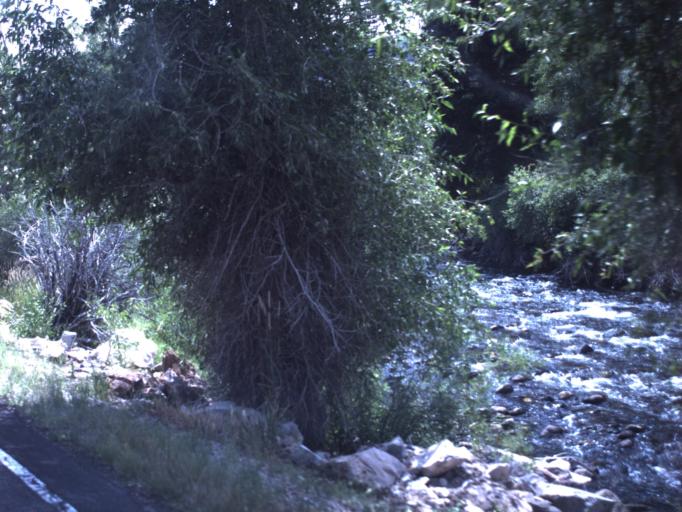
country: US
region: Utah
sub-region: Summit County
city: Francis
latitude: 40.5578
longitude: -111.1676
